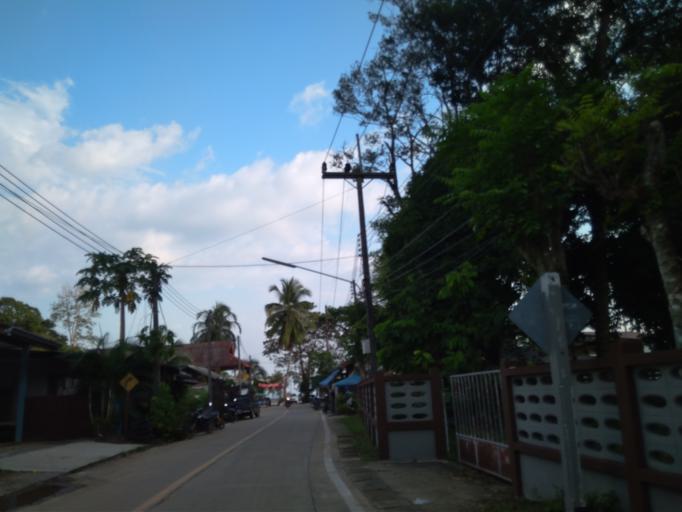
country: TH
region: Phangnga
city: Ko Yao
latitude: 8.1357
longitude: 98.6261
